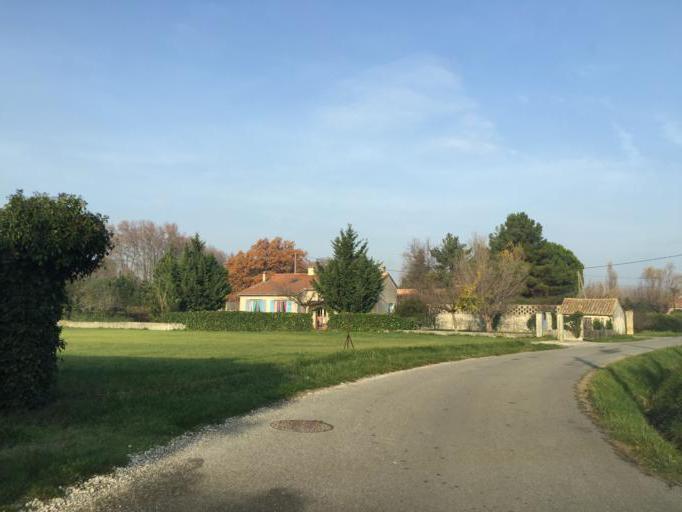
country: FR
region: Provence-Alpes-Cote d'Azur
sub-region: Departement du Vaucluse
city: Jonquieres
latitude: 44.1217
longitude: 4.8958
